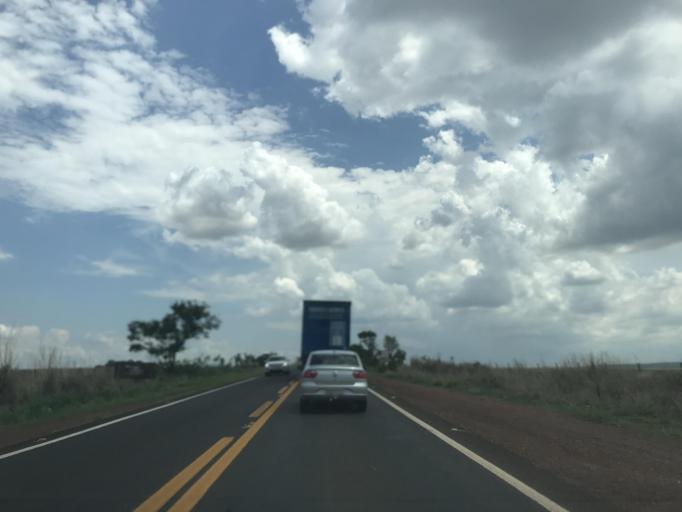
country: BR
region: Goias
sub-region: Caldas Novas
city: Caldas Novas
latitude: -17.4822
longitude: -48.7550
